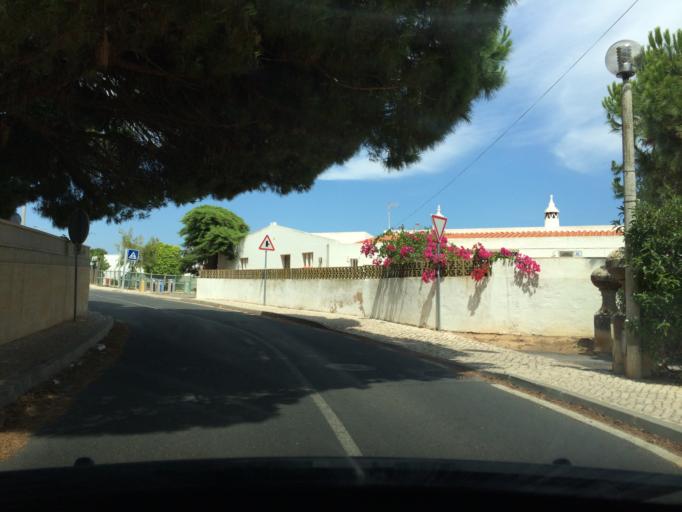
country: PT
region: Faro
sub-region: Albufeira
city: Albufeira
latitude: 37.0898
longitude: -8.1961
